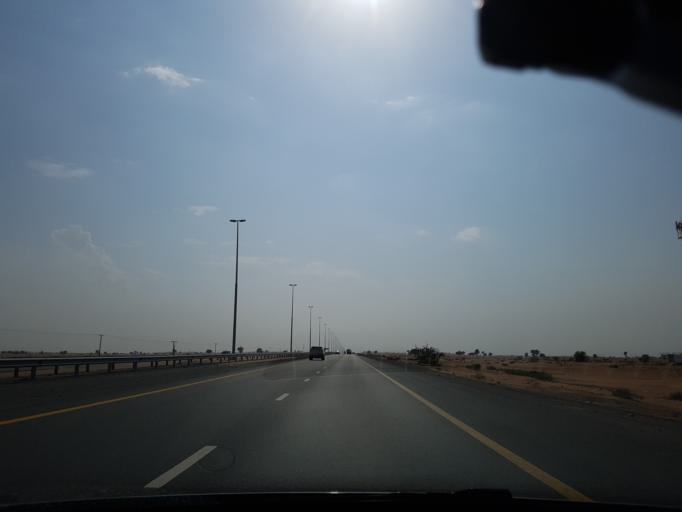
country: AE
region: Umm al Qaywayn
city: Umm al Qaywayn
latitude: 25.5365
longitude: 55.7723
